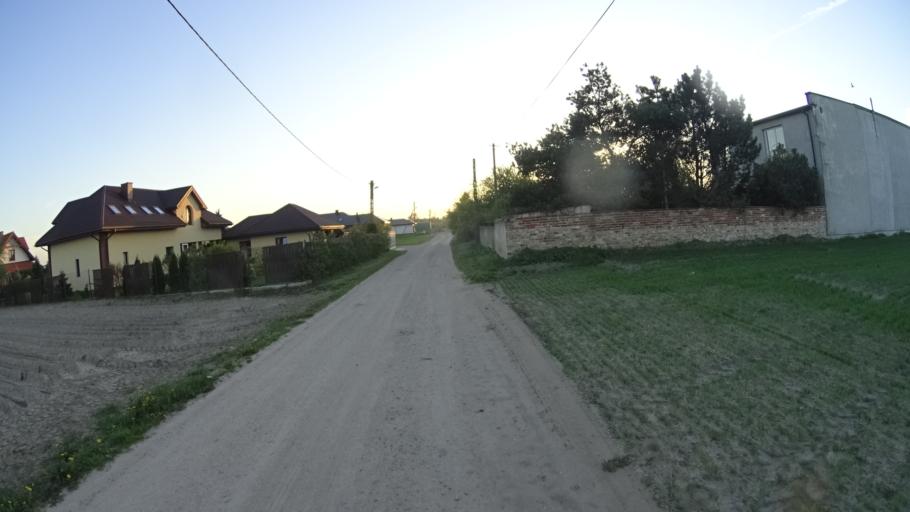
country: PL
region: Masovian Voivodeship
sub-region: Powiat warszawski zachodni
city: Ozarow Mazowiecki
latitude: 52.2294
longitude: 20.7866
